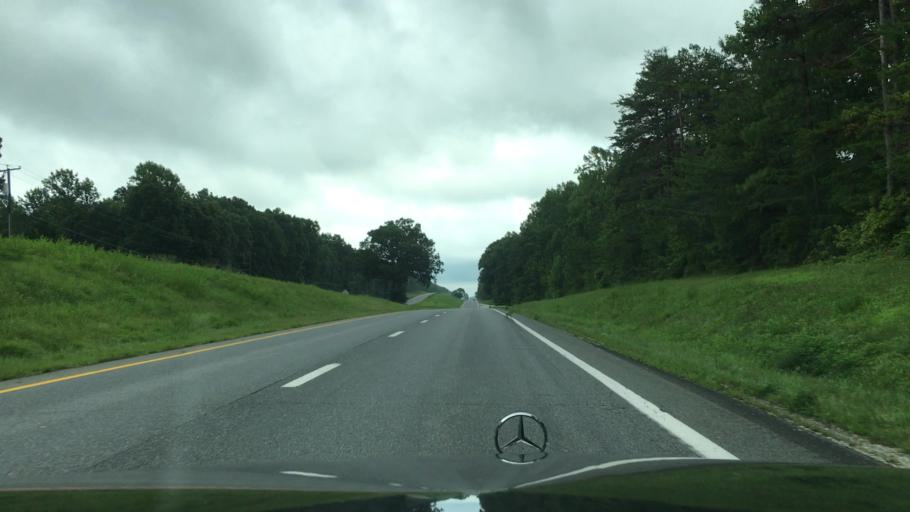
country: US
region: Virginia
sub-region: Appomattox County
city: Appomattox
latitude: 37.2869
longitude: -78.7247
